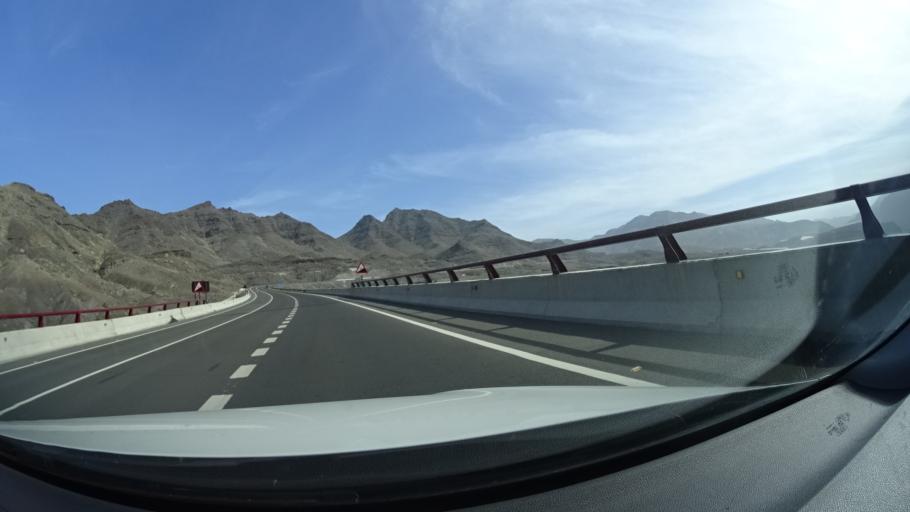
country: ES
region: Canary Islands
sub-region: Provincia de Las Palmas
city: San Nicolas
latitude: 28.0024
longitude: -15.8088
